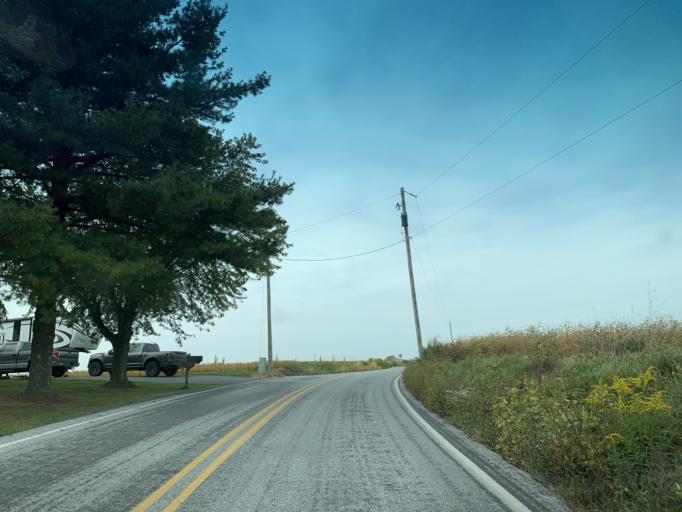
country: US
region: Pennsylvania
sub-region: York County
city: Stewartstown
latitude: 39.8063
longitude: -76.5228
